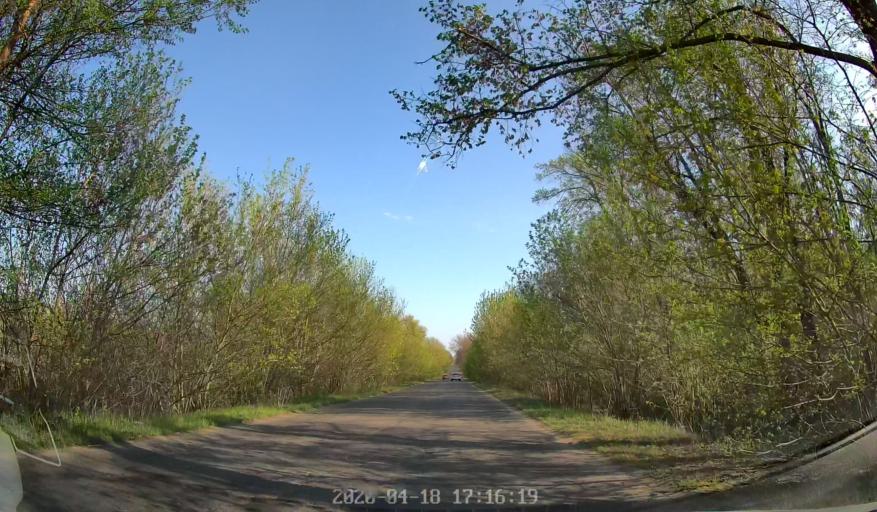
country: MD
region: Chisinau
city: Vadul lui Voda
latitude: 47.1078
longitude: 29.0628
